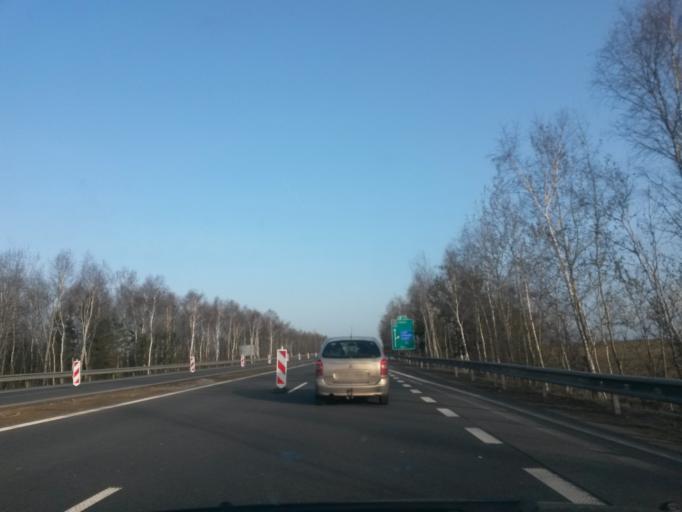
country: CZ
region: Central Bohemia
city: Stochov
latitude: 50.1557
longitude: 13.9739
